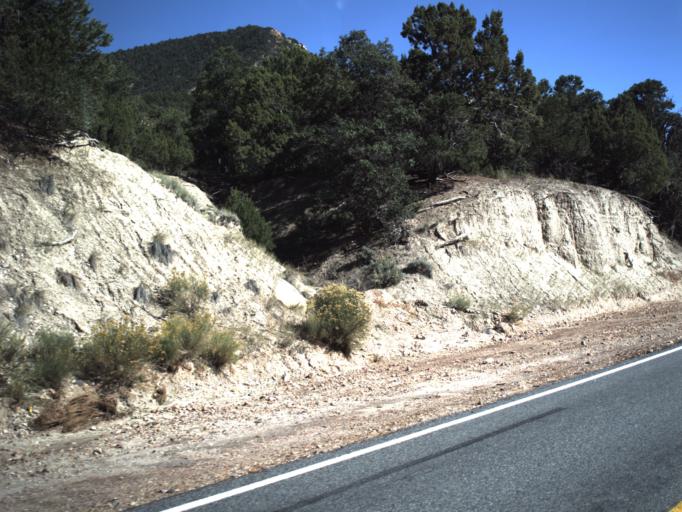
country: US
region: Utah
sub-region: Iron County
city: Parowan
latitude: 37.8276
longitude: -112.8141
